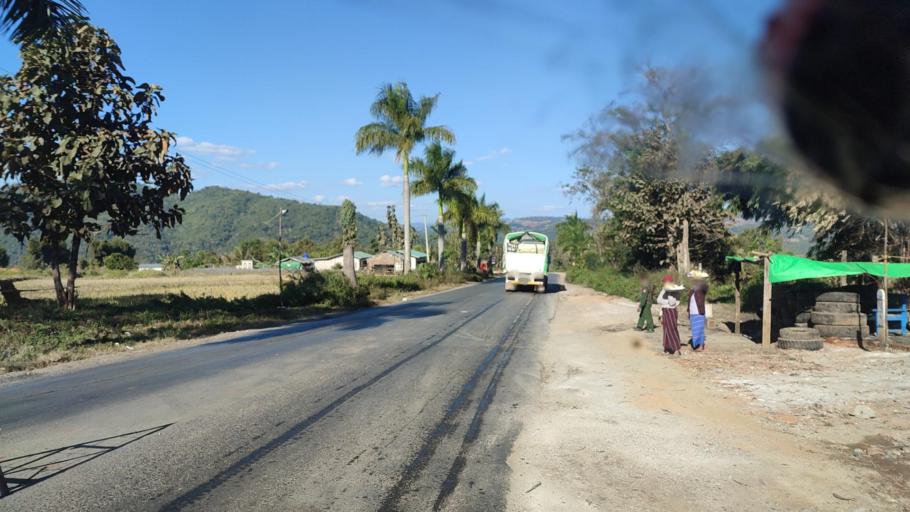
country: MM
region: Mandalay
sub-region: Pyin Oo Lwin District
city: Pyin Oo Lwin
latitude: 22.3403
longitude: 96.8160
